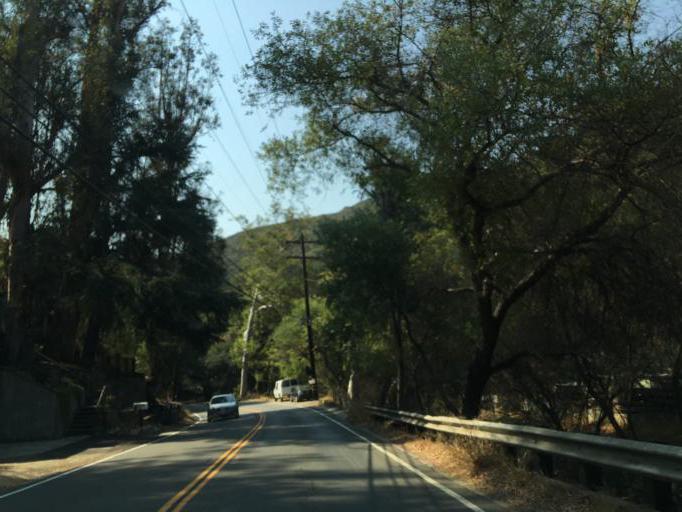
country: US
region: California
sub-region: Los Angeles County
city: Topanga
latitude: 34.1024
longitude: -118.6213
